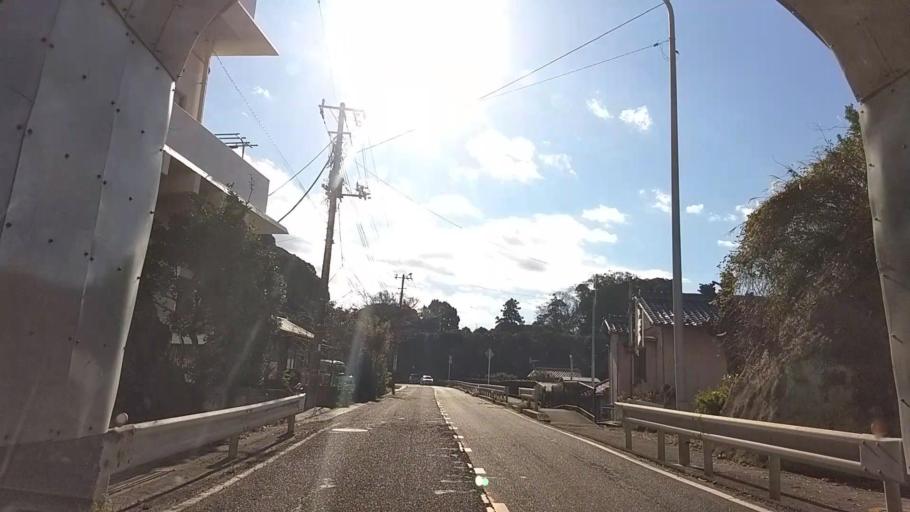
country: JP
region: Chiba
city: Tateyama
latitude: 35.0506
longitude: 139.8332
